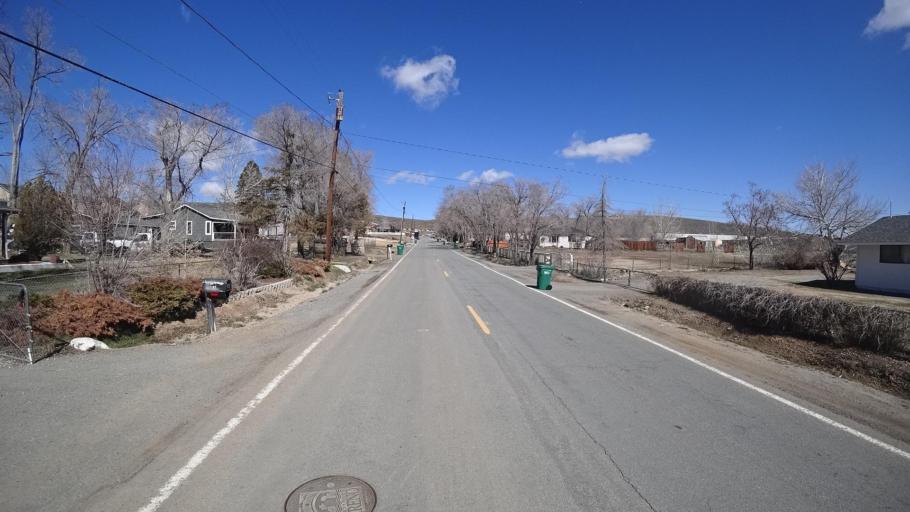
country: US
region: Nevada
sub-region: Washoe County
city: Golden Valley
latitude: 39.5904
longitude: -119.8228
